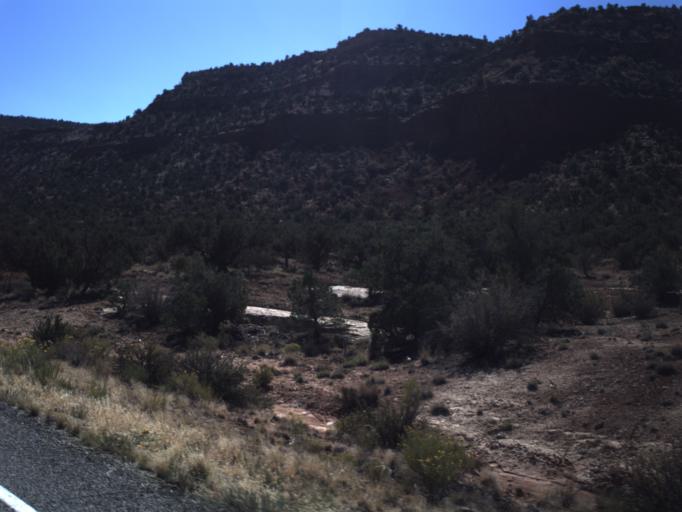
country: US
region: Utah
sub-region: San Juan County
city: Blanding
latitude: 37.6364
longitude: -110.1059
